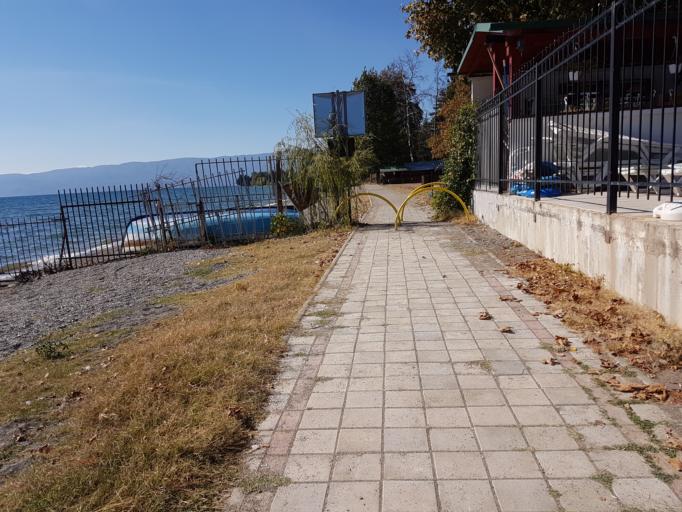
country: MK
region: Ohrid
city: Ohrid
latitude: 41.1196
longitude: 20.7833
